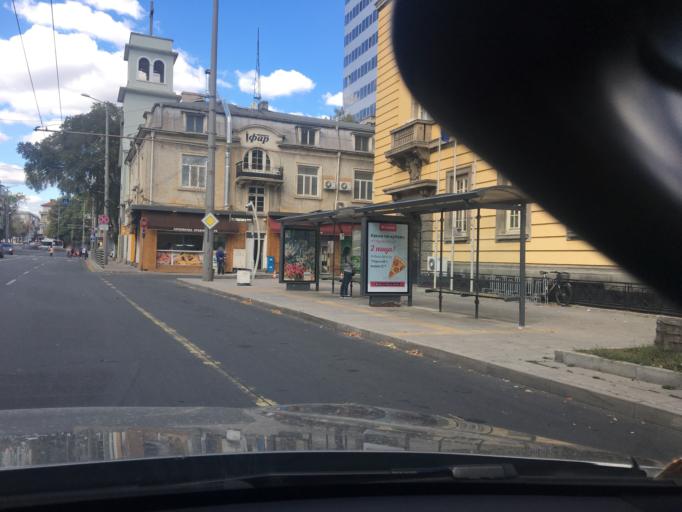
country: BG
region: Burgas
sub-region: Obshtina Burgas
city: Burgas
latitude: 42.4917
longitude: 27.4718
